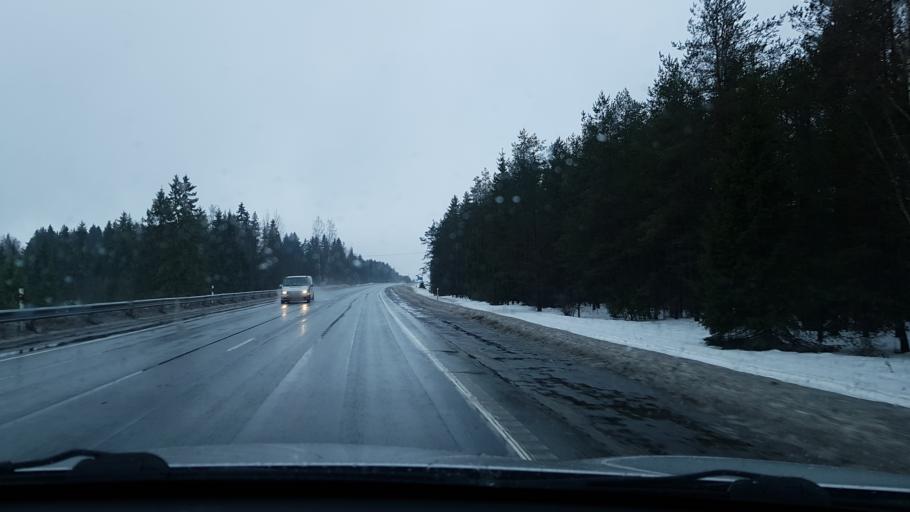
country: EE
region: Raplamaa
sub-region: Kohila vald
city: Kohila
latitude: 59.1881
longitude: 24.7869
